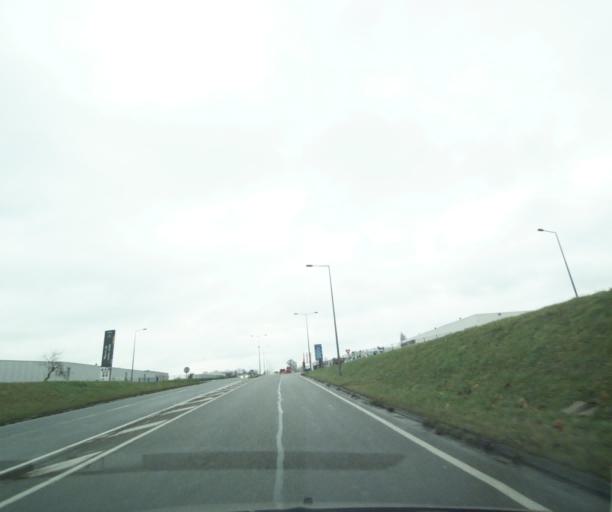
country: FR
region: Nord-Pas-de-Calais
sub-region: Departement du Nord
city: Prouvy
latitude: 50.3343
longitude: 3.4569
